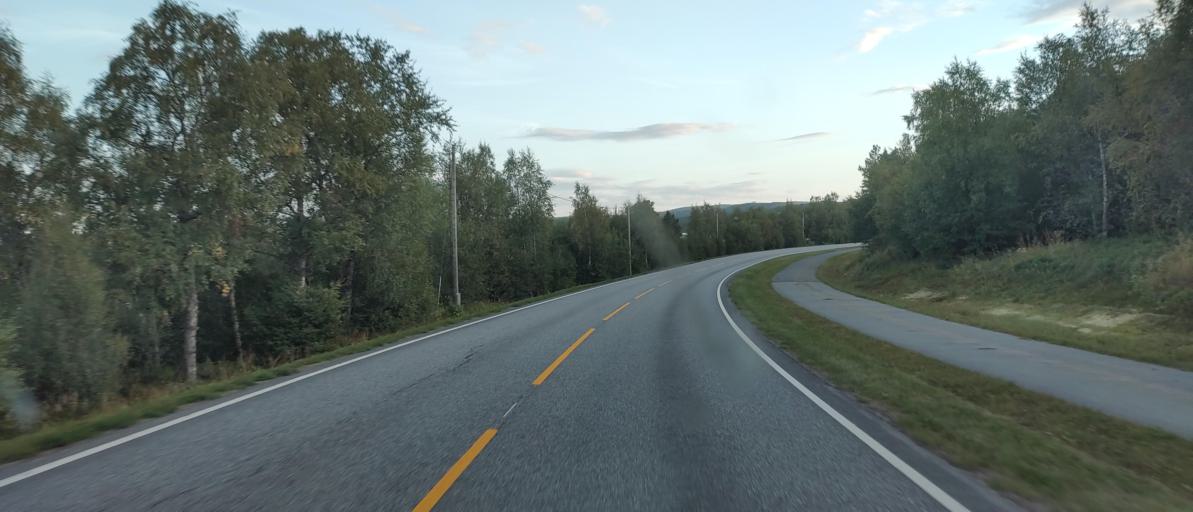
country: NO
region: Nordland
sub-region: Lodingen
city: Lodingen
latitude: 68.1952
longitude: 16.0580
